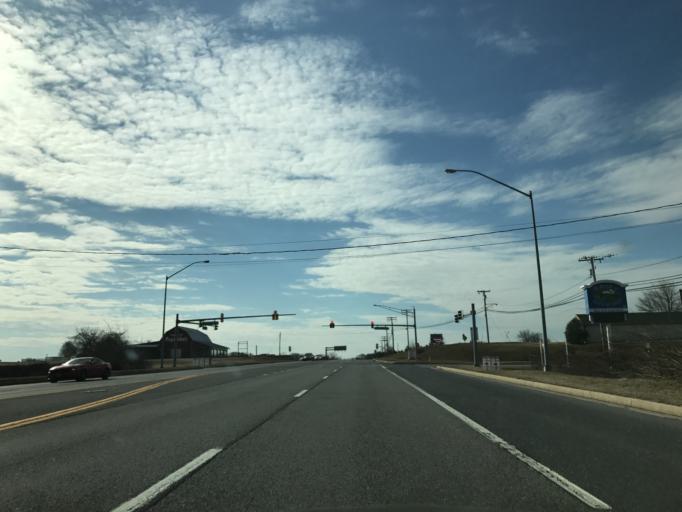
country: US
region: Maryland
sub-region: Anne Arundel County
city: South Gate
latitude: 39.1255
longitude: -76.6427
